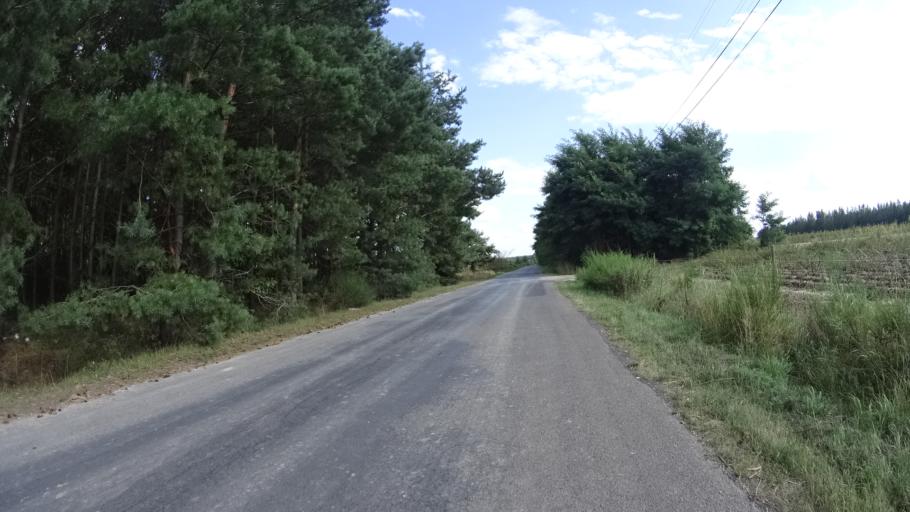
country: PL
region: Masovian Voivodeship
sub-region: Powiat grojecki
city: Mogielnica
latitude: 51.6856
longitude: 20.7559
